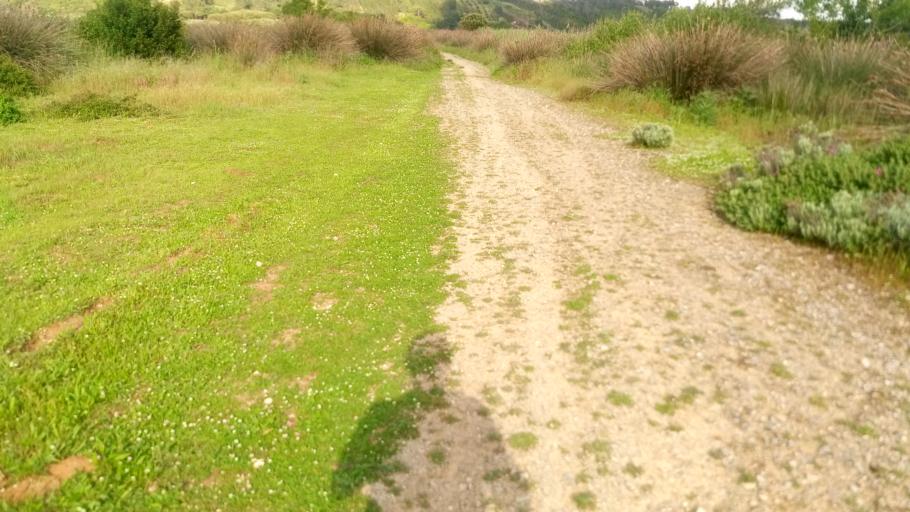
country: PT
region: Leiria
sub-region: Obidos
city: Obidos
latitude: 39.3964
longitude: -9.2039
